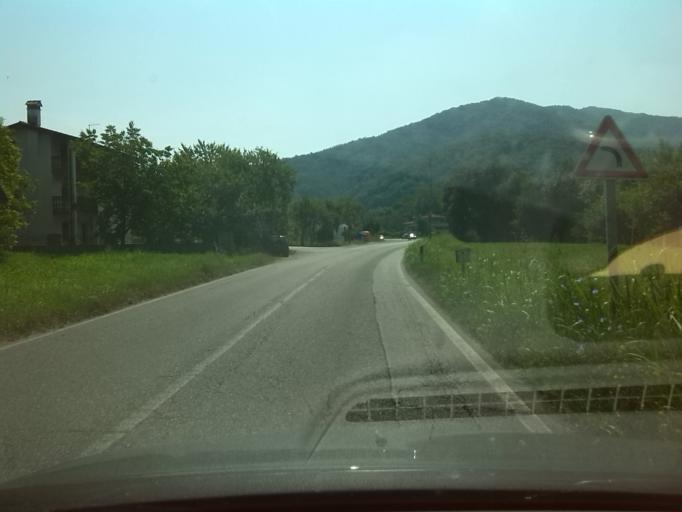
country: IT
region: Friuli Venezia Giulia
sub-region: Provincia di Udine
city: San Pietro al Natisone
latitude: 46.1155
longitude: 13.4997
